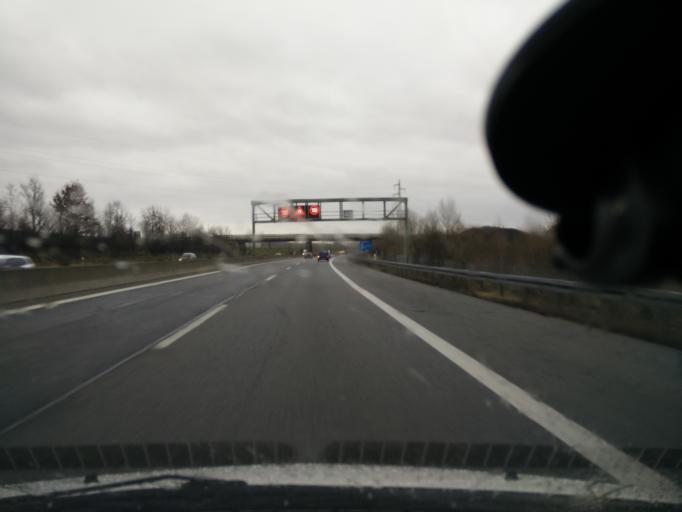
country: DE
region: Bavaria
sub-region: Upper Bavaria
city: Karlsfeld
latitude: 48.1917
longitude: 11.4376
